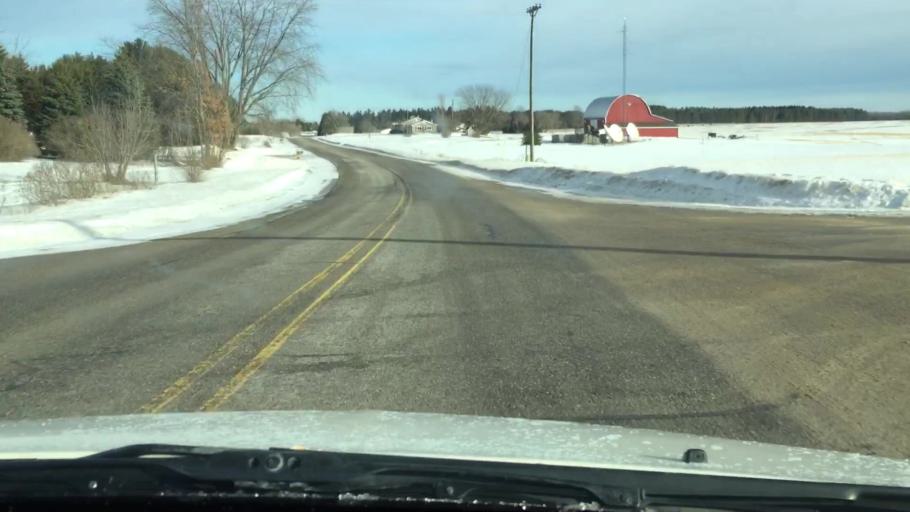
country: US
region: Michigan
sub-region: Kalkaska County
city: Kalkaska
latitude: 44.6403
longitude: -85.2103
